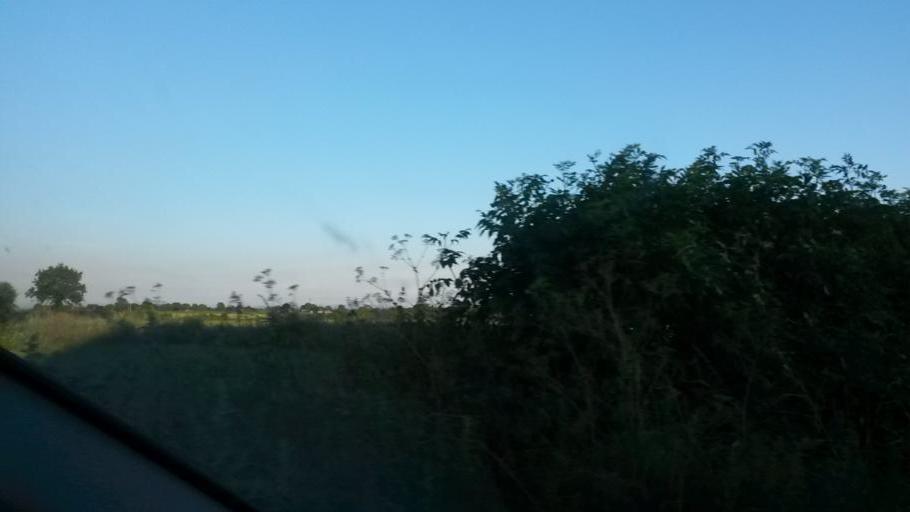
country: IE
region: Leinster
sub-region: An Mhi
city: Ashbourne
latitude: 53.5453
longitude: -6.3603
